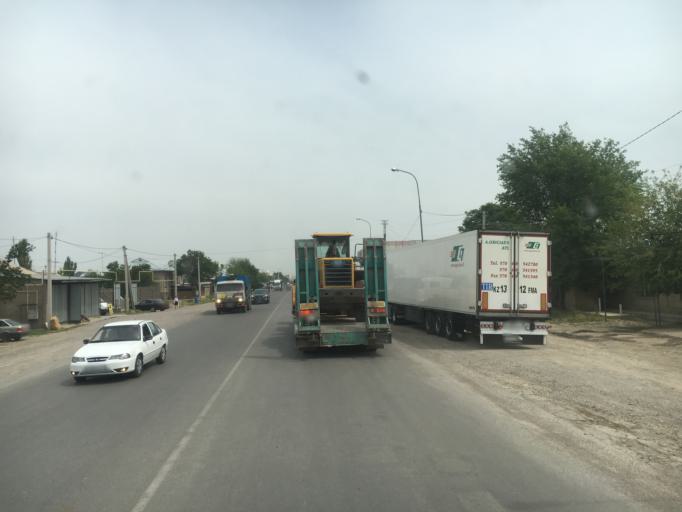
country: KZ
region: Ongtustik Qazaqstan
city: Shymkent
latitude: 42.3382
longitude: 69.5202
